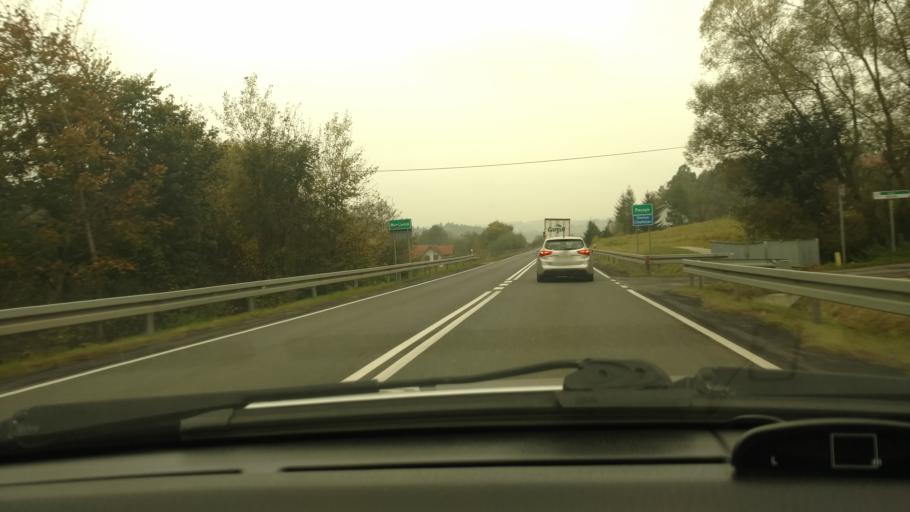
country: PL
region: Lesser Poland Voivodeship
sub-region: Powiat nowosadecki
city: Kamionka Wielka
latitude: 49.6158
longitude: 20.8078
